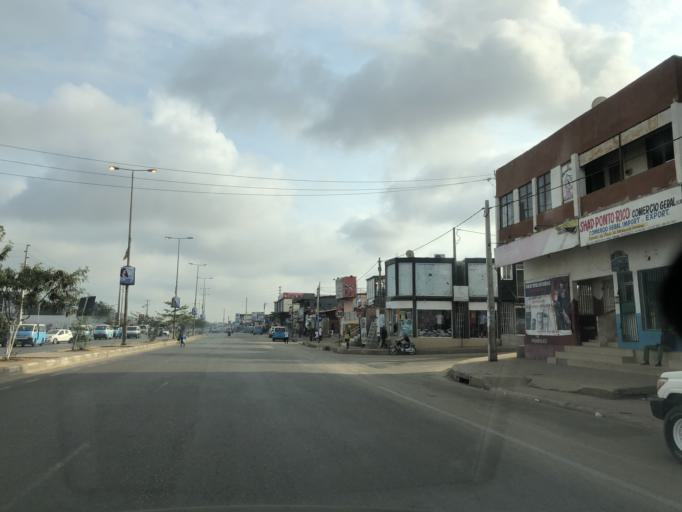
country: AO
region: Luanda
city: Luanda
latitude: -8.8830
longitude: 13.2081
